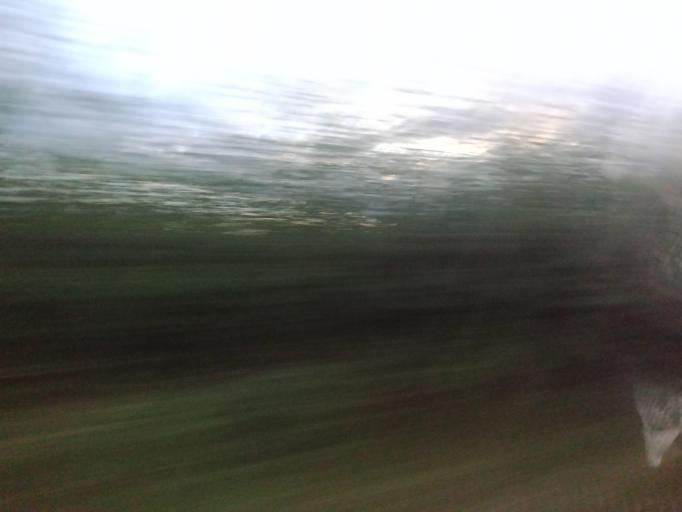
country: IE
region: Leinster
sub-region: Laois
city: Mountmellick
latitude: 53.1855
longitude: -7.4007
